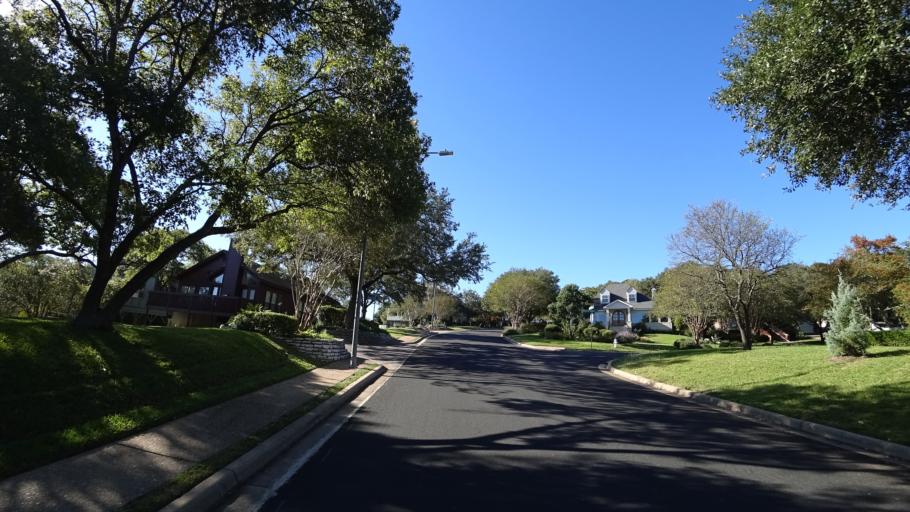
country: US
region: Texas
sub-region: Travis County
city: West Lake Hills
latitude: 30.3325
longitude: -97.8011
